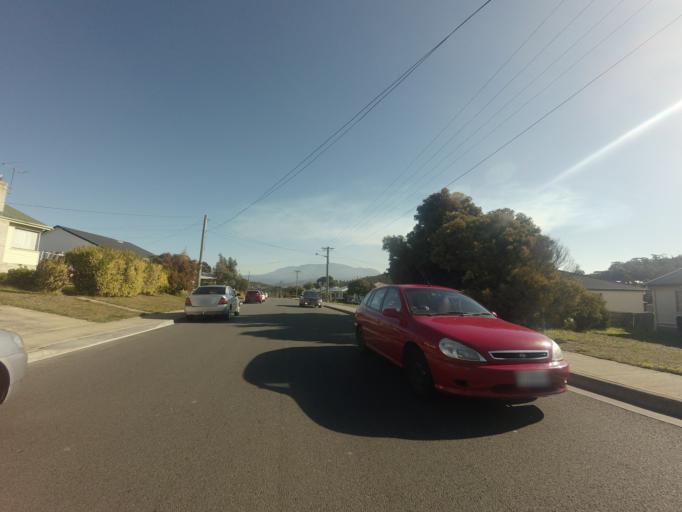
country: AU
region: Tasmania
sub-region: Clarence
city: Warrane
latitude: -42.8576
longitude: 147.3800
